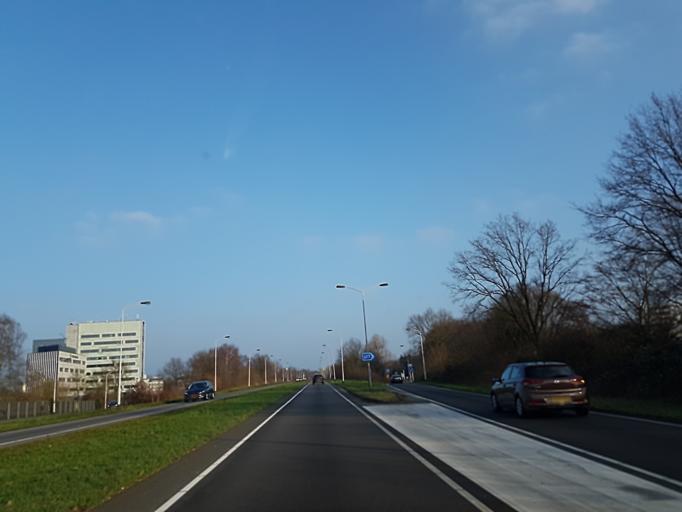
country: NL
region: North Brabant
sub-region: Gemeente Breda
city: Breda
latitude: 51.5785
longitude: 4.8011
